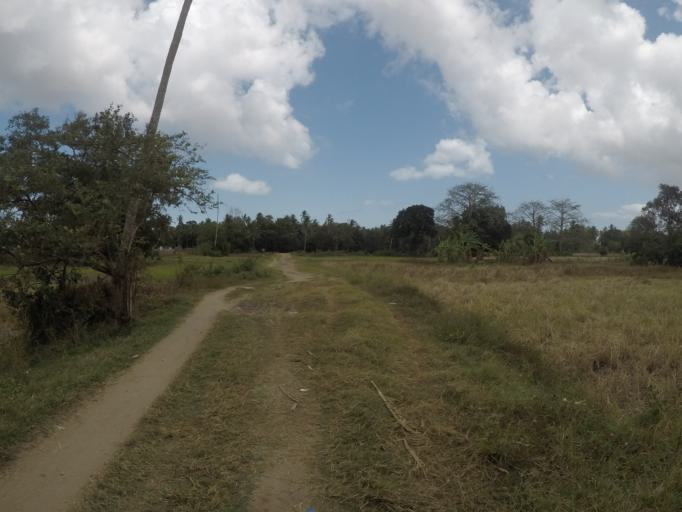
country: TZ
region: Zanzibar Urban/West
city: Zanzibar
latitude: -6.2053
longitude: 39.2411
